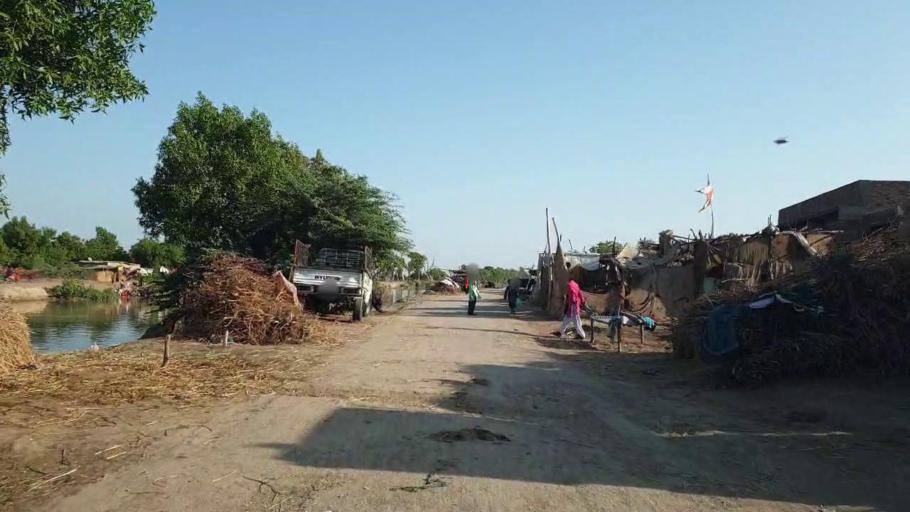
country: PK
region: Sindh
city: Hyderabad
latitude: 25.3237
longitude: 68.4266
